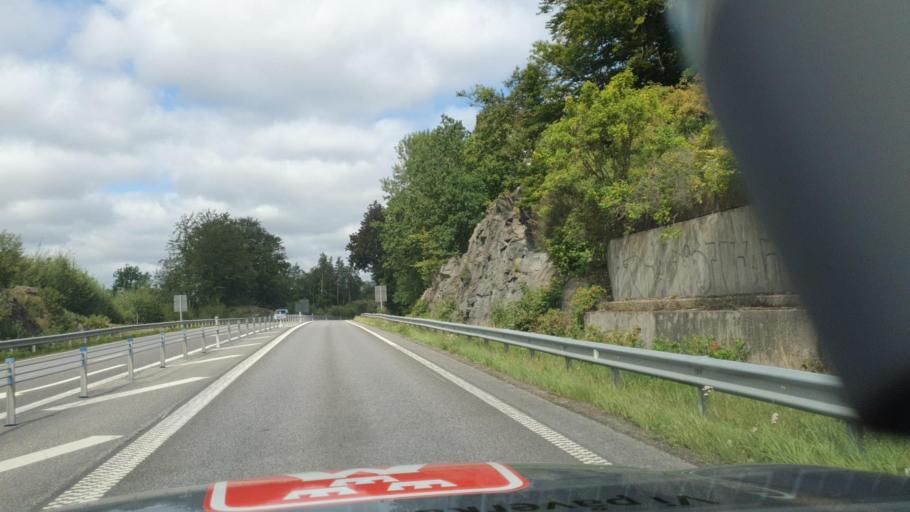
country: SE
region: Blekinge
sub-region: Karlskrona Kommun
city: Rodeby
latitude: 56.2306
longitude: 15.6275
